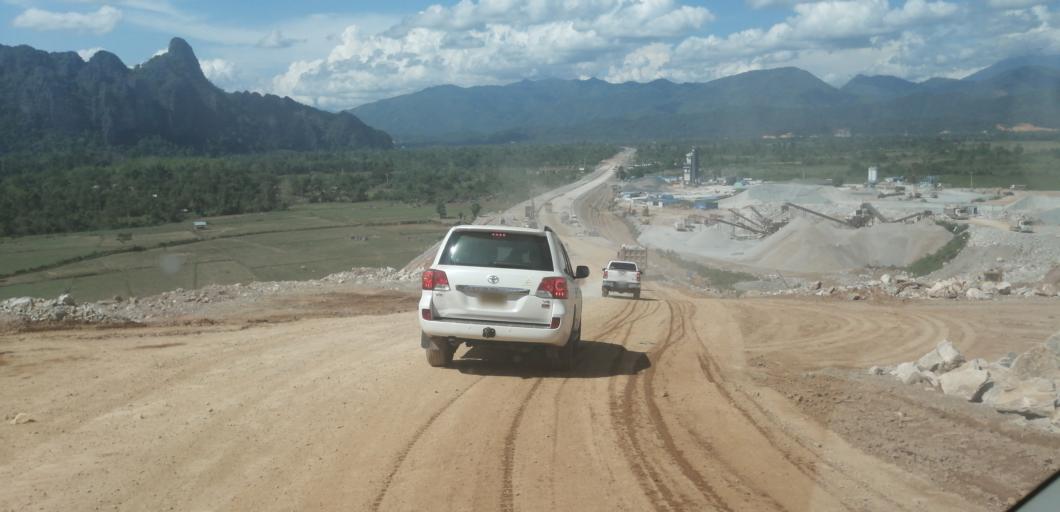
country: LA
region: Vientiane
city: Vangviang
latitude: 18.8715
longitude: 102.4285
